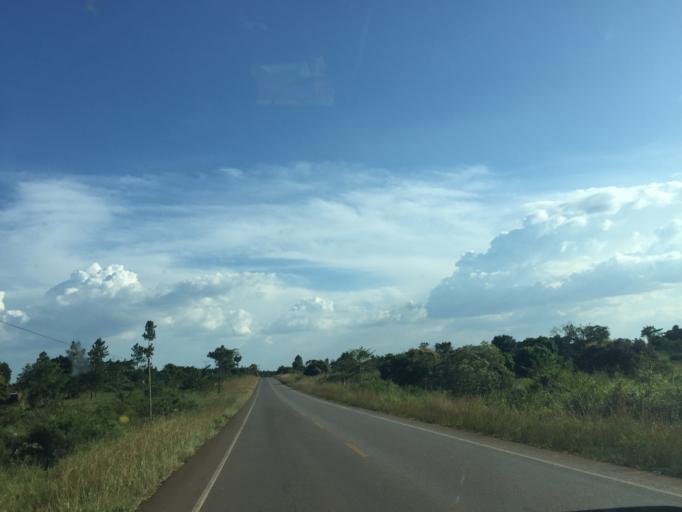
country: UG
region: Central Region
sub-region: Nakasongola District
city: Nakasongola
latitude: 1.2299
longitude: 32.4642
